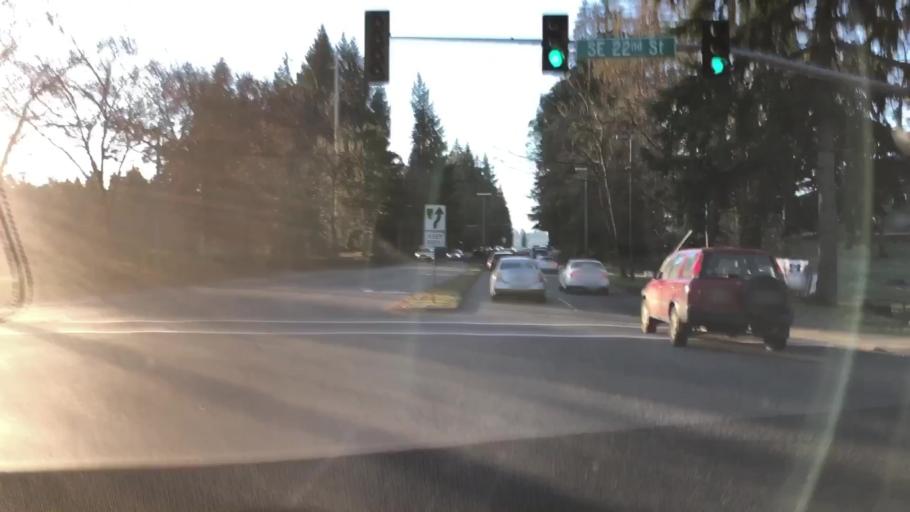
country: US
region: Washington
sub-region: King County
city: Eastgate
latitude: 47.5909
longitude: -122.1428
